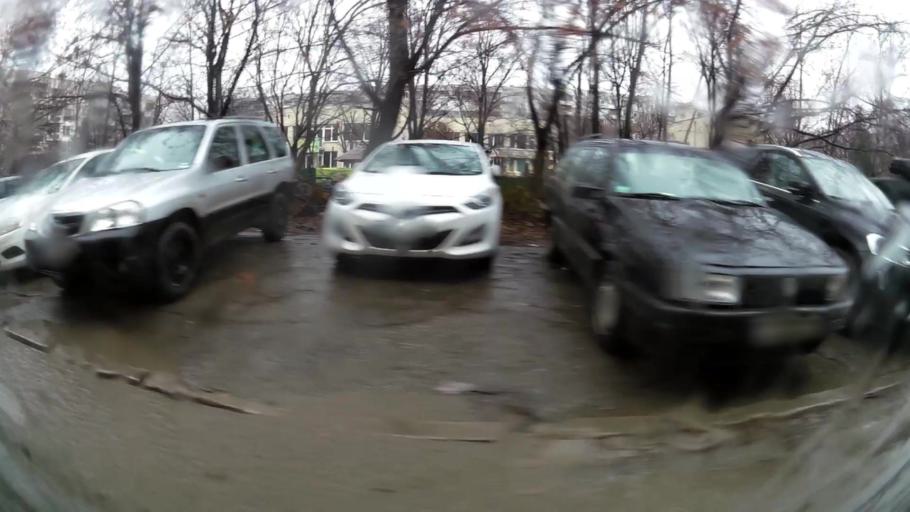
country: BG
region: Sofia-Capital
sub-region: Stolichna Obshtina
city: Sofia
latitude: 42.6519
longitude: 23.3761
